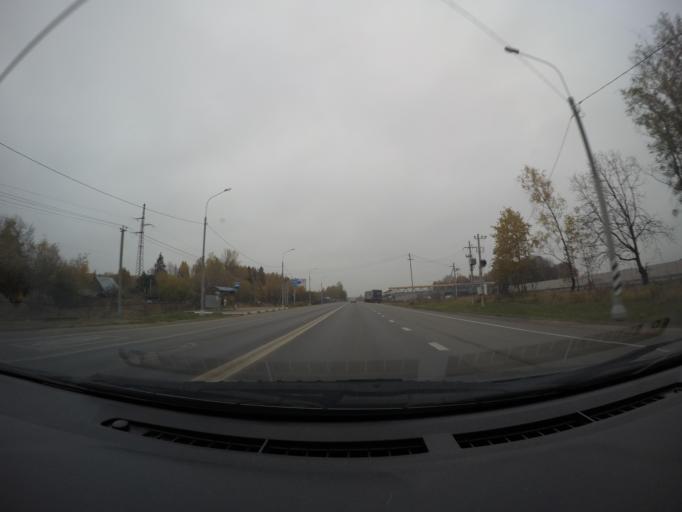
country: RU
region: Moskovskaya
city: Vostryakovo
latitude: 55.3362
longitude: 37.7828
